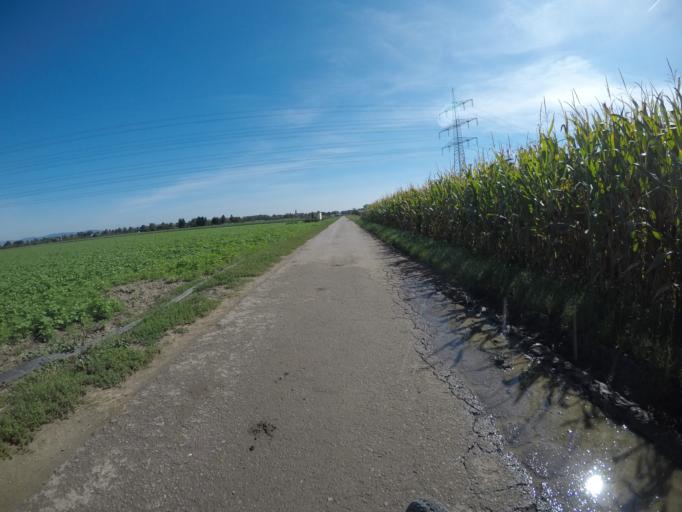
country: DE
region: Hesse
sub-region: Regierungsbezirk Darmstadt
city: Burstadt
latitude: 49.6485
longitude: 8.4368
